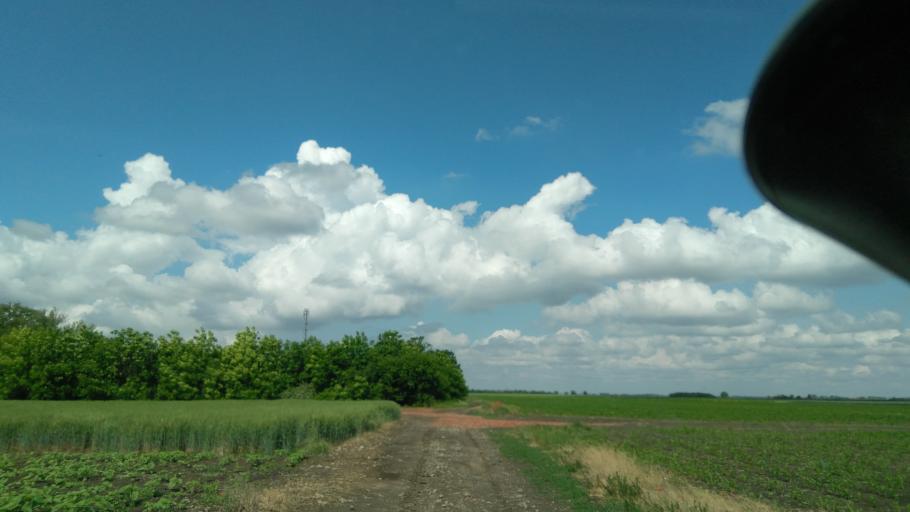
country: HU
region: Bekes
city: Mezobereny
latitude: 46.8339
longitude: 21.0105
